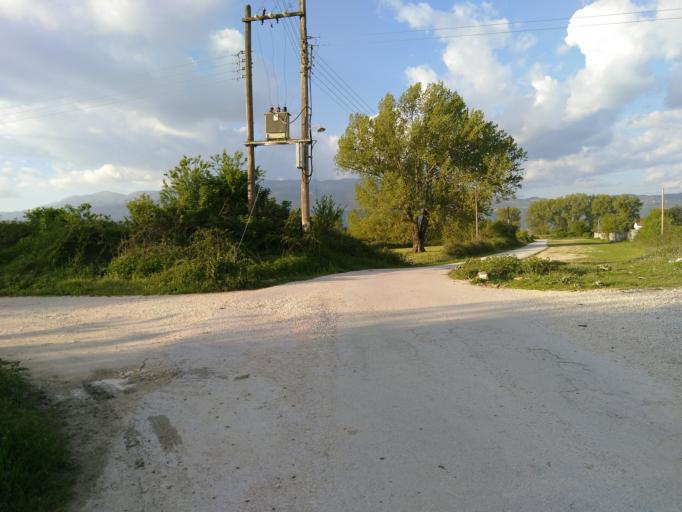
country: GR
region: Epirus
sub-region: Nomos Ioanninon
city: Katsikas
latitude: 39.6274
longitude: 20.8887
